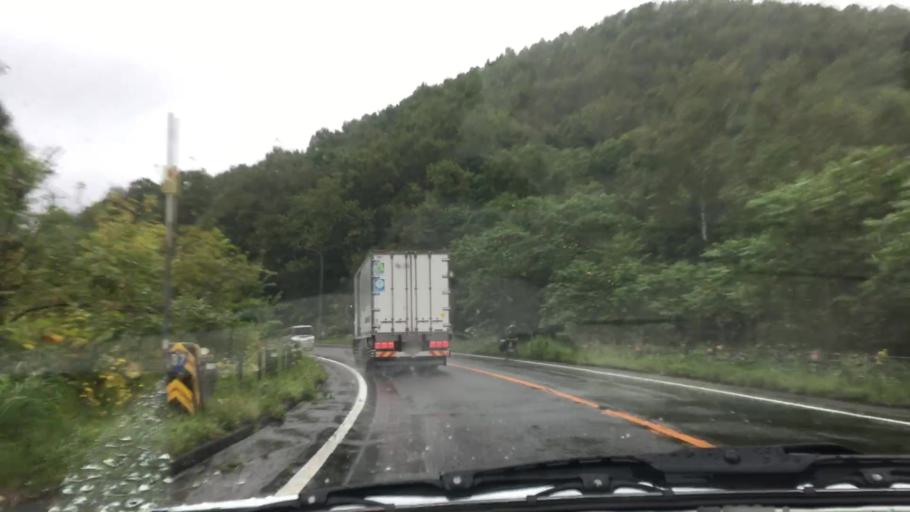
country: JP
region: Hokkaido
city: Niseko Town
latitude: 42.5977
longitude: 140.6721
